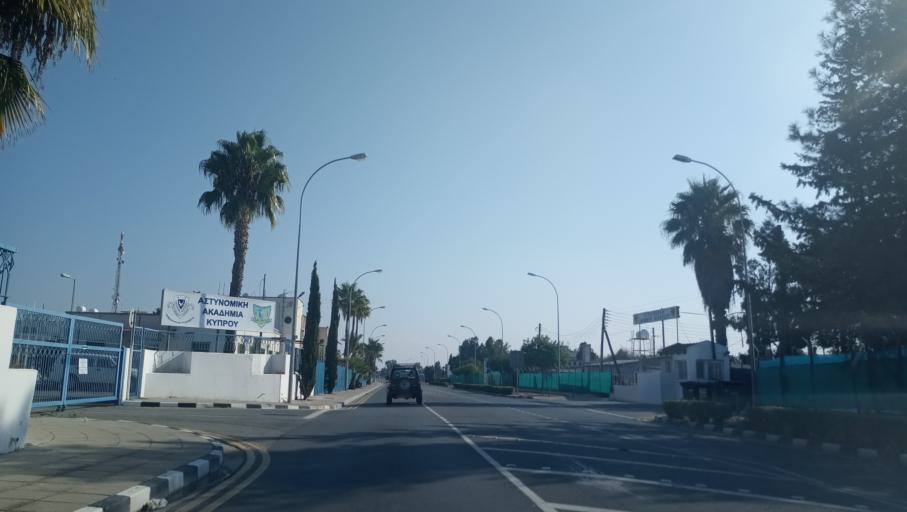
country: CY
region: Lefkosia
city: Nicosia
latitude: 35.1447
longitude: 33.3781
